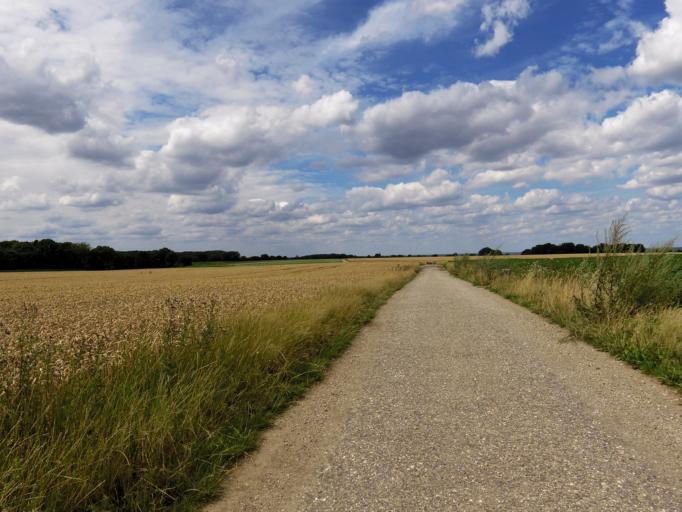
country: NL
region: Limburg
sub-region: Gemeente Schinnen
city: Doenrade
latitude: 50.9798
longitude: 5.9010
